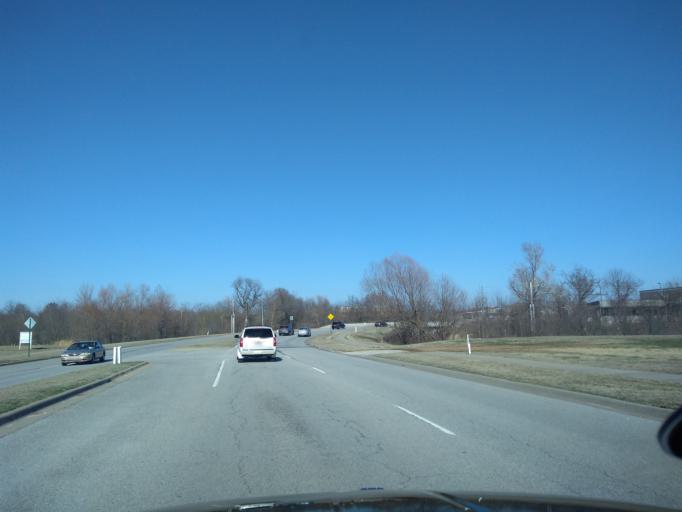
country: US
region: Arkansas
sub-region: Washington County
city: Johnson
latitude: 36.1172
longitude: -94.1622
